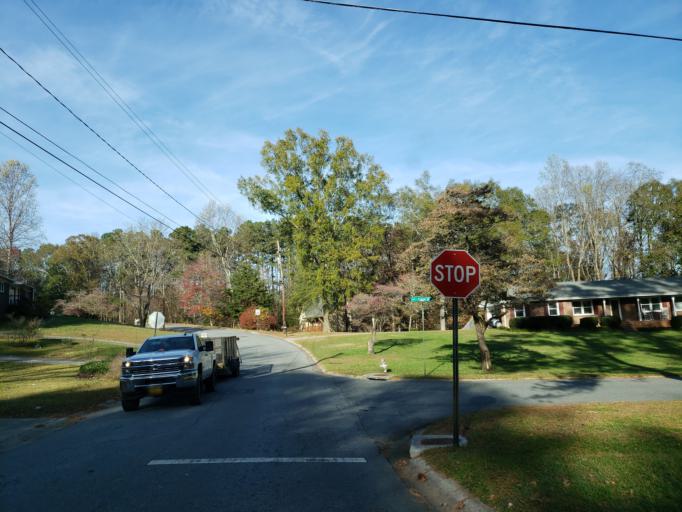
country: US
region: Georgia
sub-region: Cobb County
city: Kennesaw
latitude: 34.0275
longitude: -84.6067
